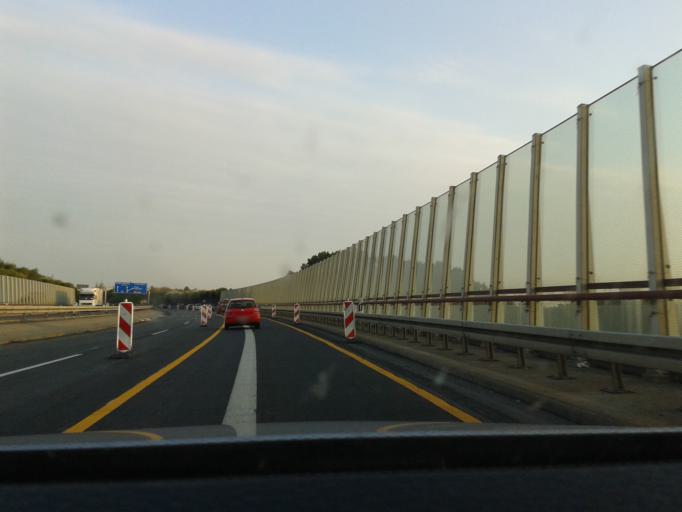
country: DE
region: Saxony
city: Freital
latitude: 51.0442
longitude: 13.6075
